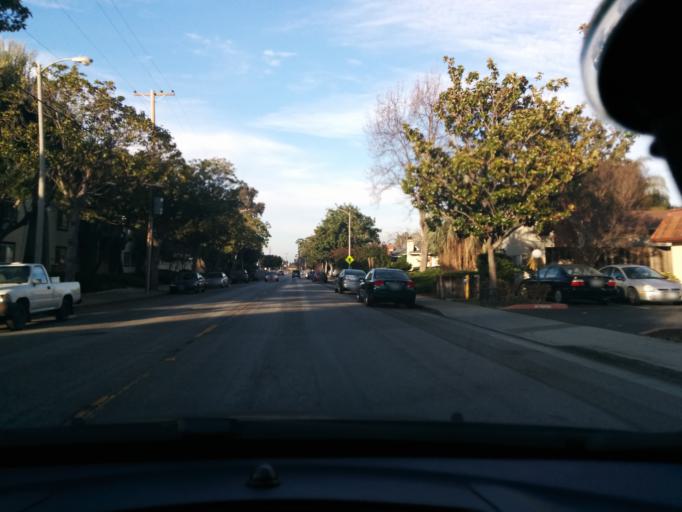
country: US
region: California
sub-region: Santa Clara County
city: Sunnyvale
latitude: 37.3819
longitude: -122.0536
